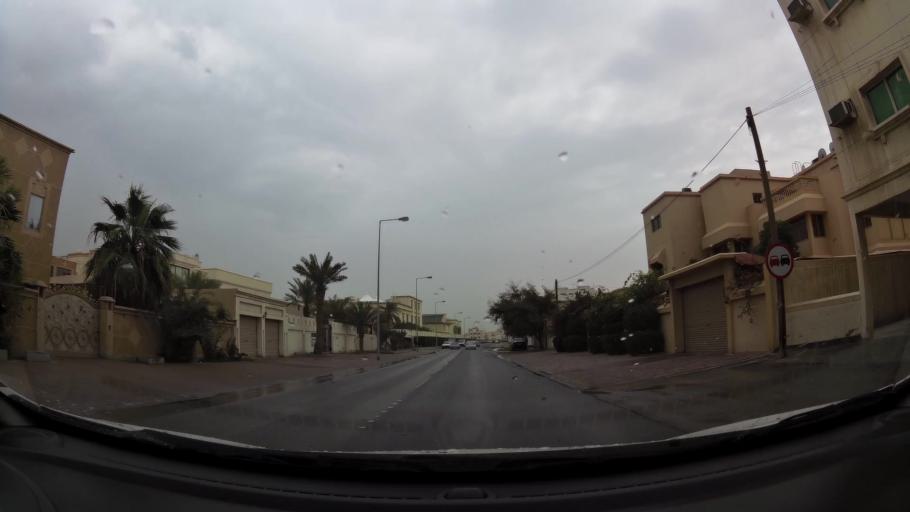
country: BH
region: Northern
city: Ar Rifa'
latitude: 26.1554
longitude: 50.5786
